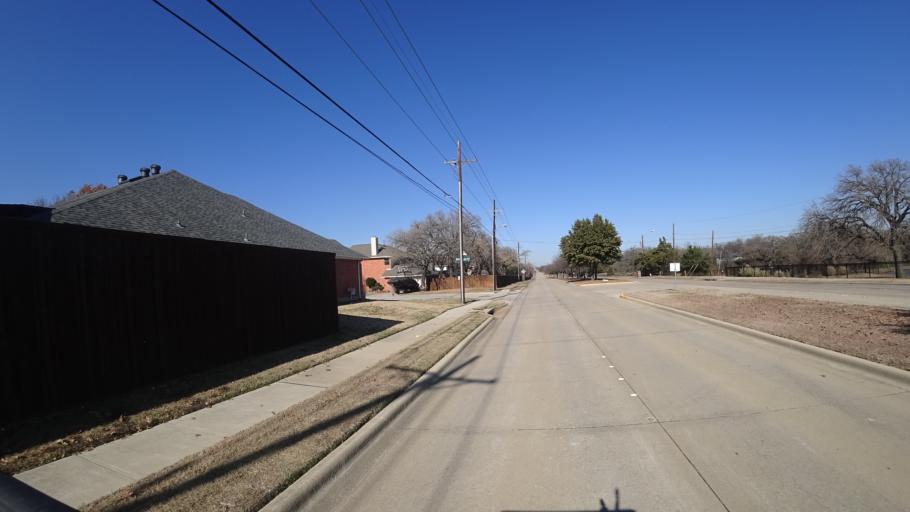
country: US
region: Texas
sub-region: Denton County
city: Lewisville
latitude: 33.0134
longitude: -97.0193
